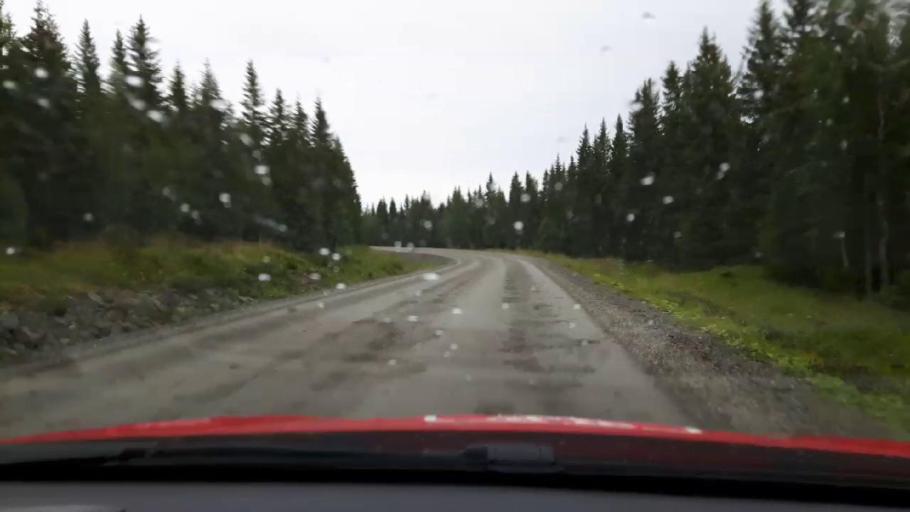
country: SE
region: Jaemtland
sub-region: Are Kommun
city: Are
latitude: 63.4506
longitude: 12.6545
